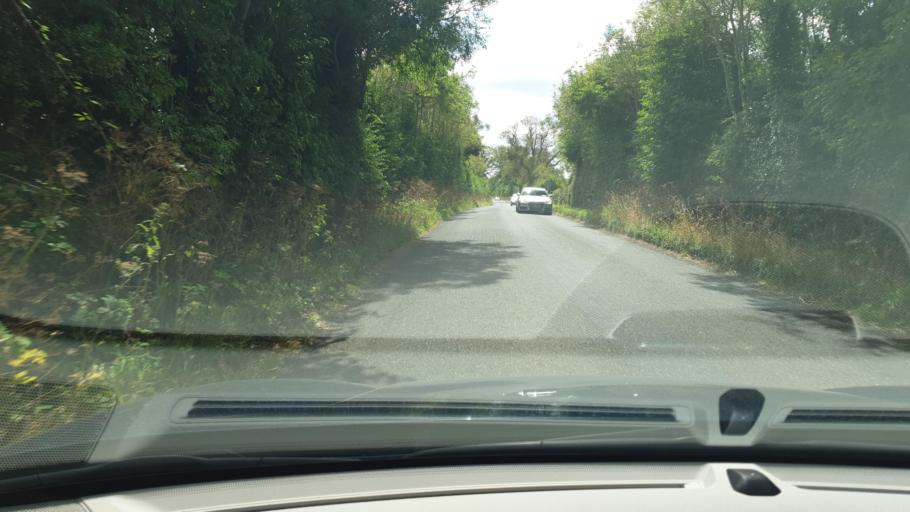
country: IE
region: Leinster
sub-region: An Mhi
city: Dunshaughlin
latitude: 53.5504
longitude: -6.6128
